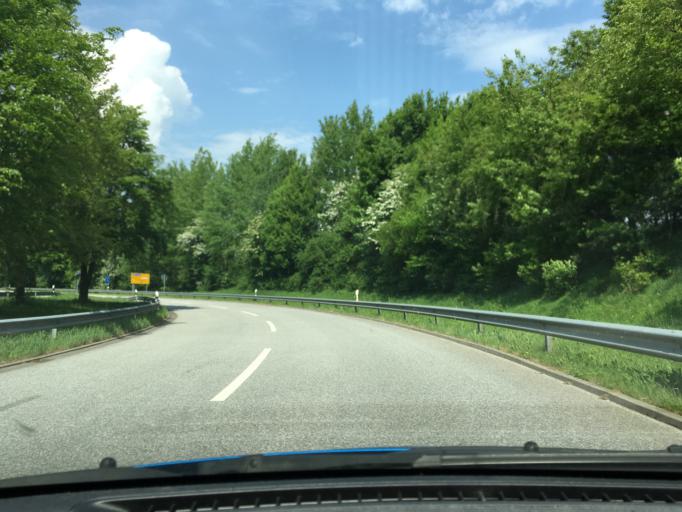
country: DE
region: Lower Saxony
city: Seevetal
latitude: 53.4332
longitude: 9.9359
